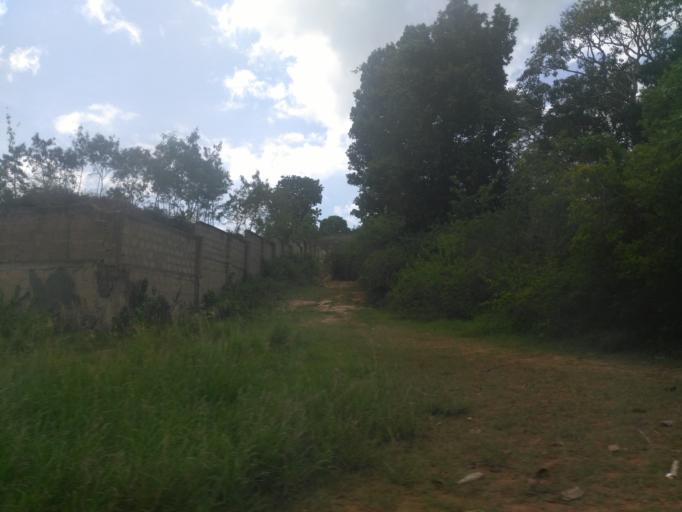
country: TZ
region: Zanzibar Urban/West
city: Zanzibar
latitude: -6.2758
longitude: 39.2722
